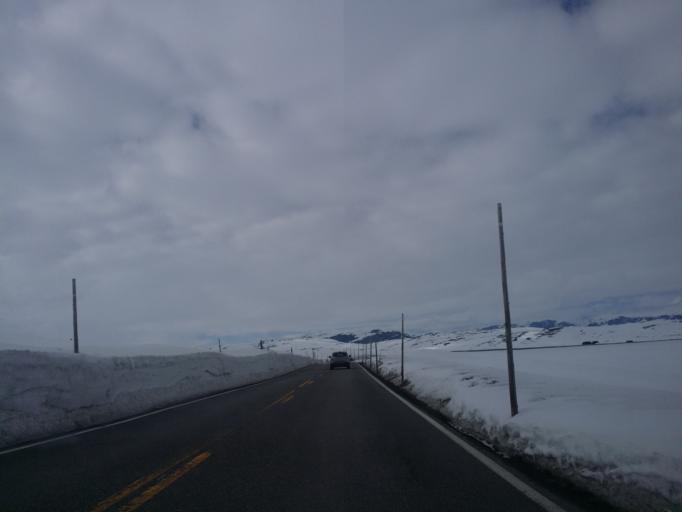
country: NO
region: Buskerud
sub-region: Hol
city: Geilo
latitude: 60.4529
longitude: 7.8192
